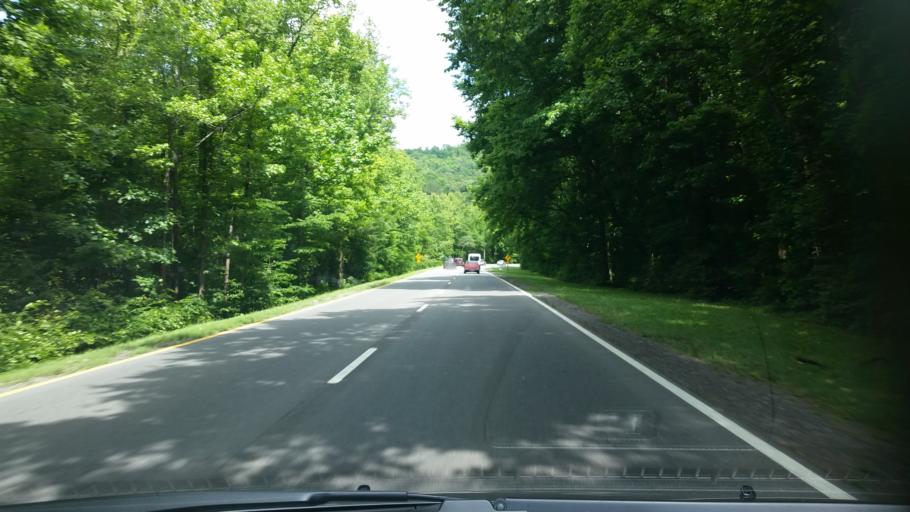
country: US
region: Tennessee
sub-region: Sevier County
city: Gatlinburg
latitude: 35.7364
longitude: -83.5212
